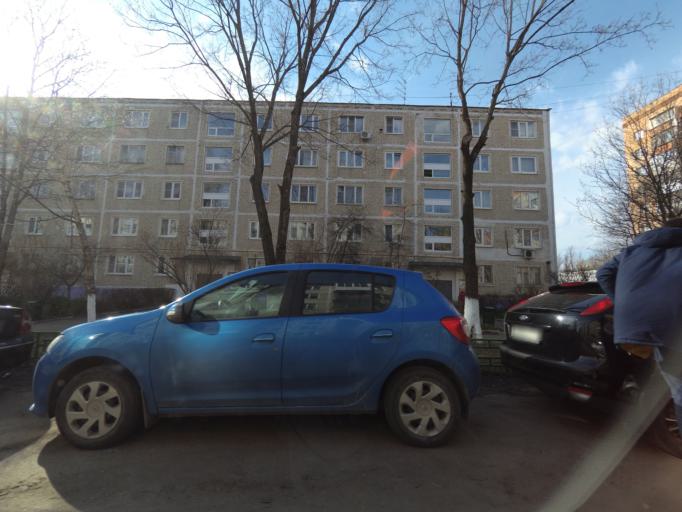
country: RU
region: Moskovskaya
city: Lugovaya
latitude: 56.0472
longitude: 37.4858
